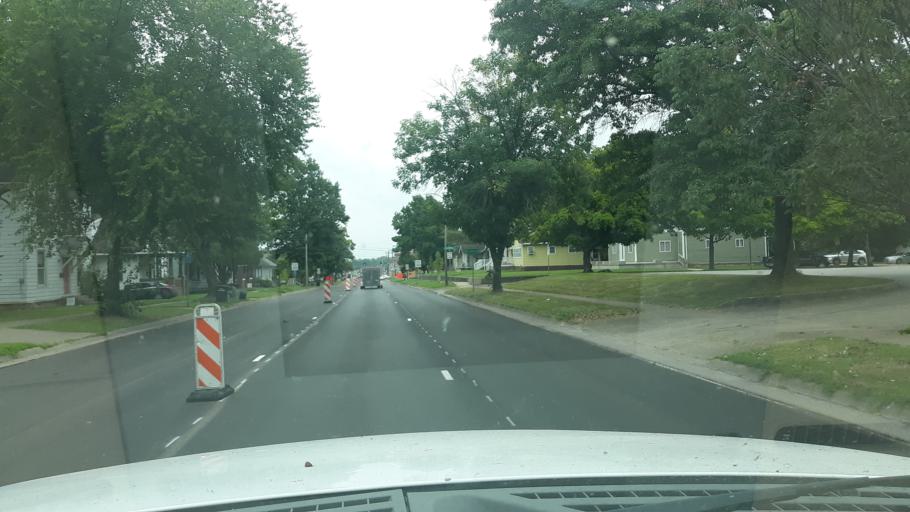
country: US
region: Illinois
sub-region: Jackson County
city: Carbondale
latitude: 37.7249
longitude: -89.2216
